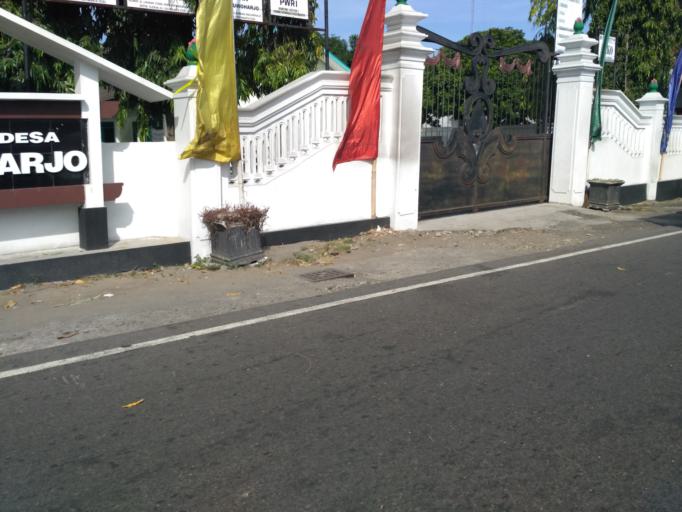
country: ID
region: Daerah Istimewa Yogyakarta
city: Depok
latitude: -7.7826
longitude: 110.4299
